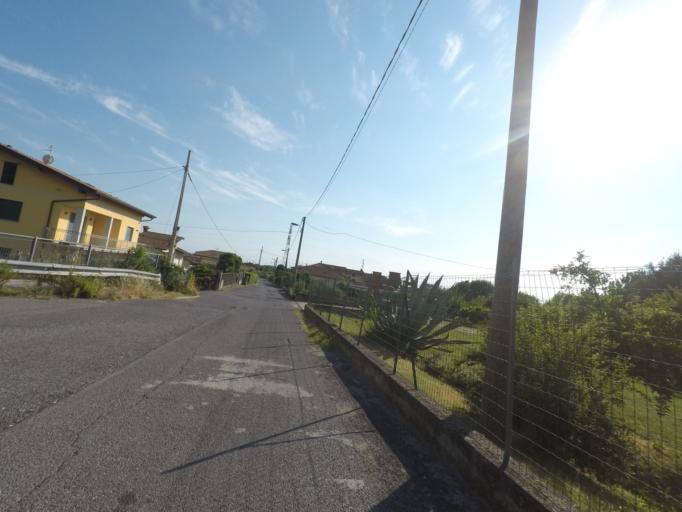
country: IT
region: Tuscany
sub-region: Provincia di Massa-Carrara
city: Capanne-Prato-Cinquale
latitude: 44.0177
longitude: 10.1433
